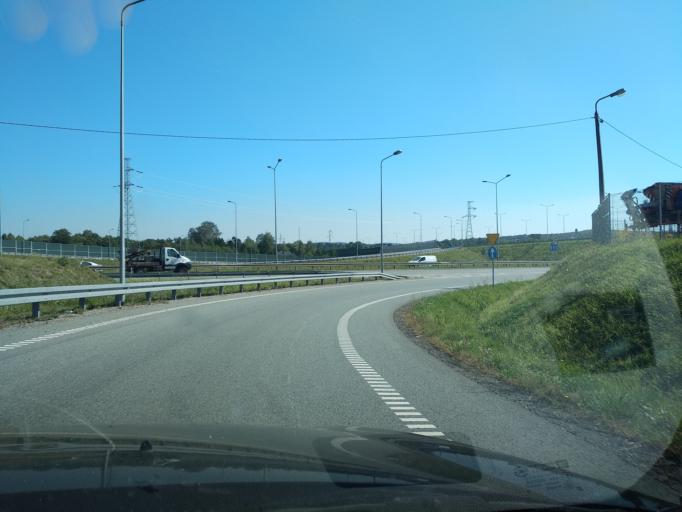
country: PL
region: Swietokrzyskie
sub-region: Powiat kielecki
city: Kostomloty Drugie
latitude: 50.9094
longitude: 20.5780
